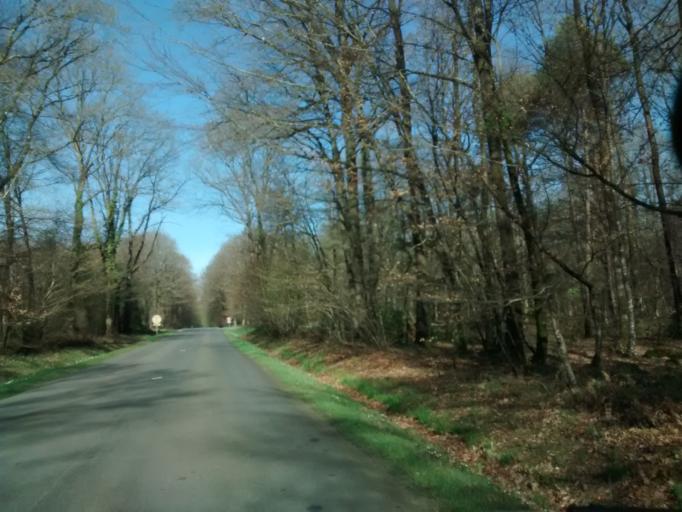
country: FR
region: Brittany
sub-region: Departement d'Ille-et-Vilaine
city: Liffre
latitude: 48.2072
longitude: -1.5440
